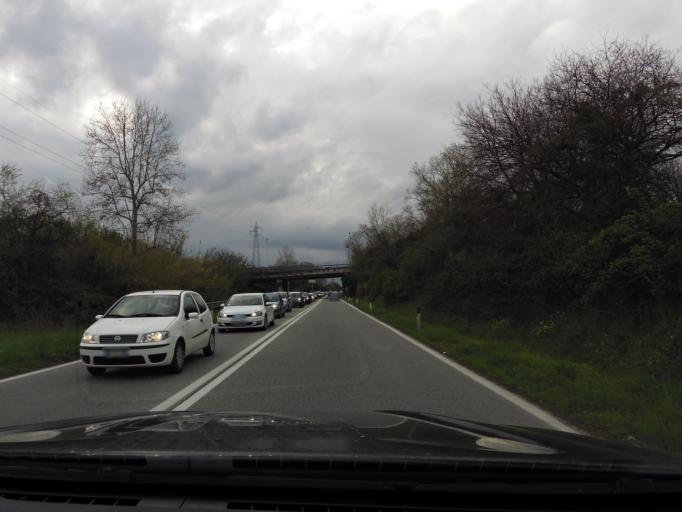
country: IT
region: The Marches
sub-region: Provincia di Macerata
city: Porto Recanati
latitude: 43.4380
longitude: 13.6412
